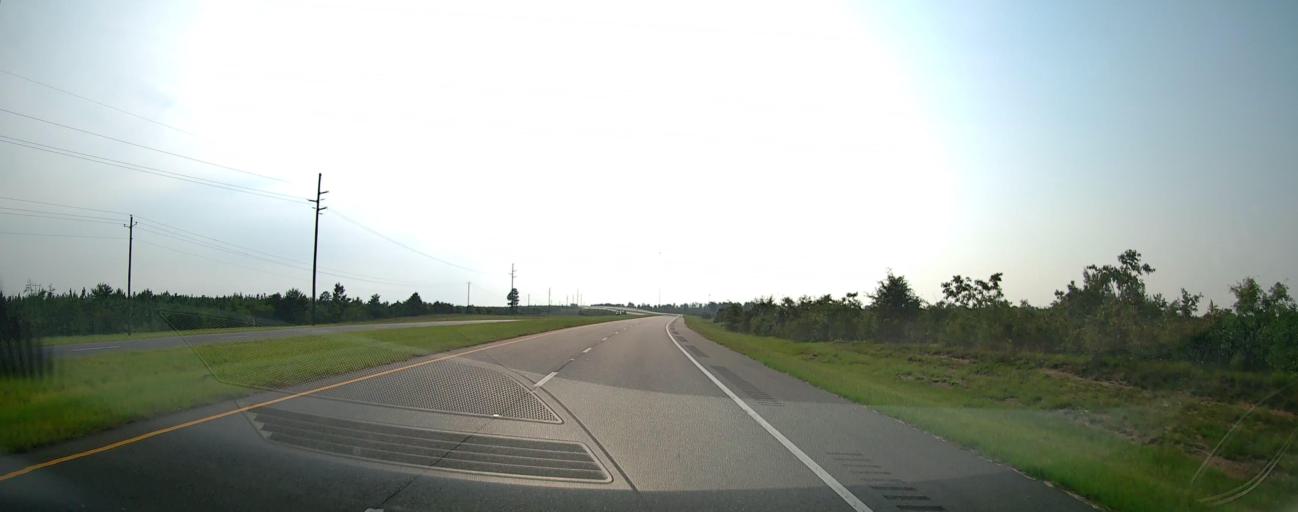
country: US
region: Georgia
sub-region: Talbot County
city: Talbotton
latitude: 32.5954
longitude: -84.4405
